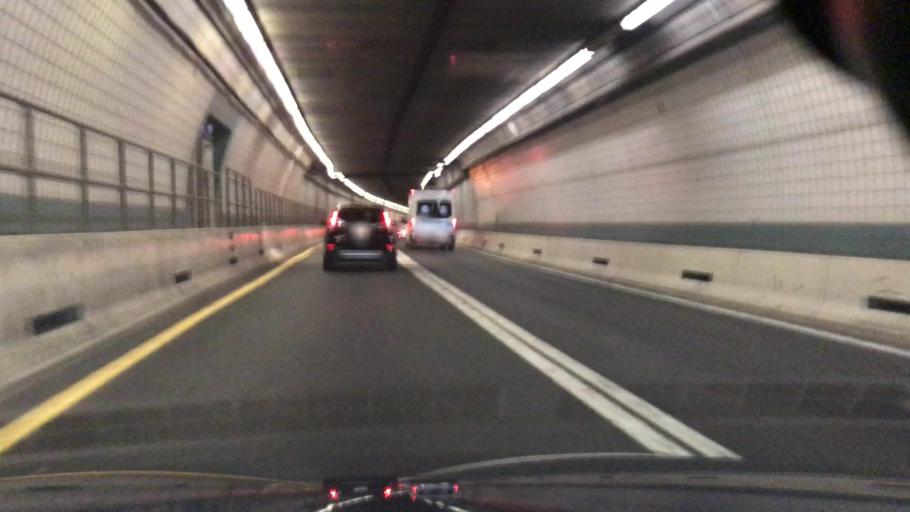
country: US
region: Massachusetts
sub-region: Suffolk County
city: South Boston
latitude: 42.3540
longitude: -71.0217
